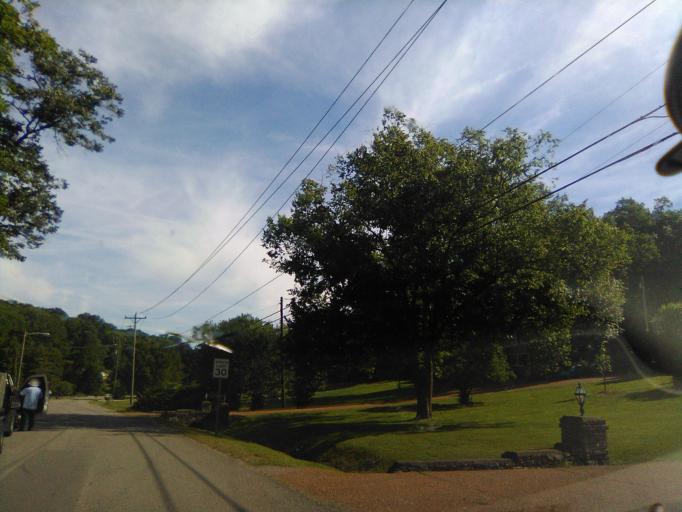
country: US
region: Tennessee
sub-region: Davidson County
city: Belle Meade
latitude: 36.1062
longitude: -86.9111
